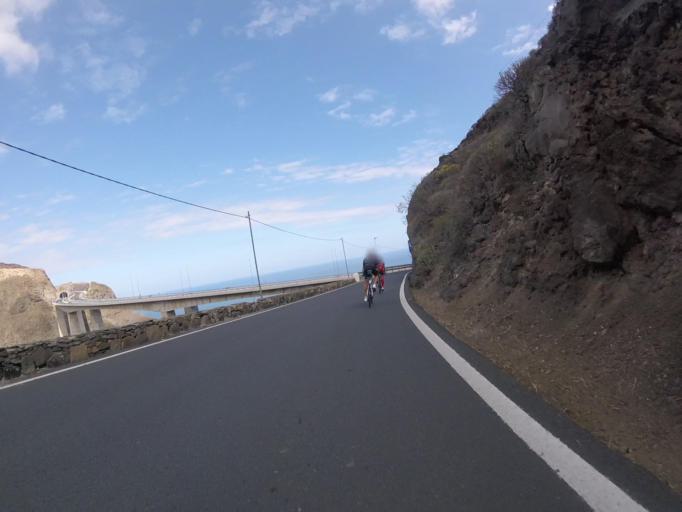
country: ES
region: Canary Islands
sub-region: Provincia de Las Palmas
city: Guia
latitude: 28.1383
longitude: -15.5968
